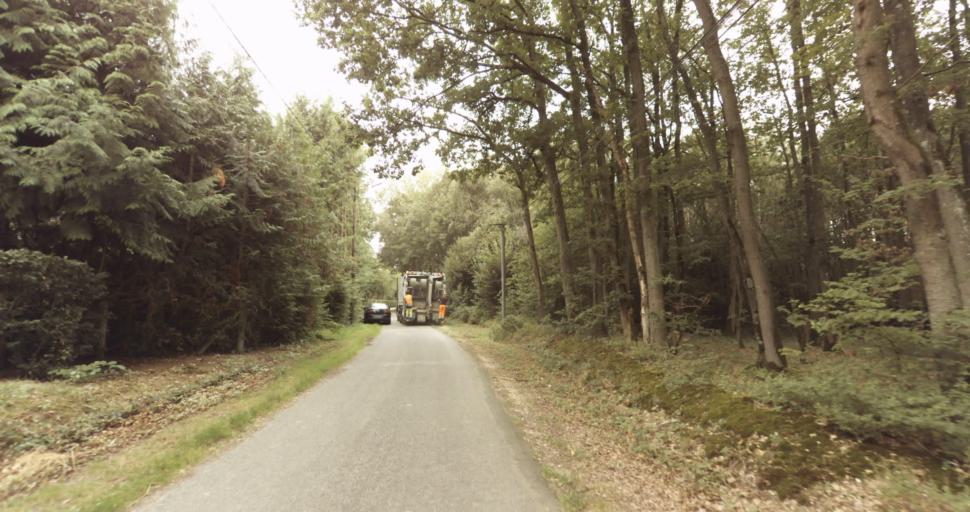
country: FR
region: Centre
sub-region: Departement d'Eure-et-Loir
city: Vert-en-Drouais
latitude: 48.7951
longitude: 1.2913
